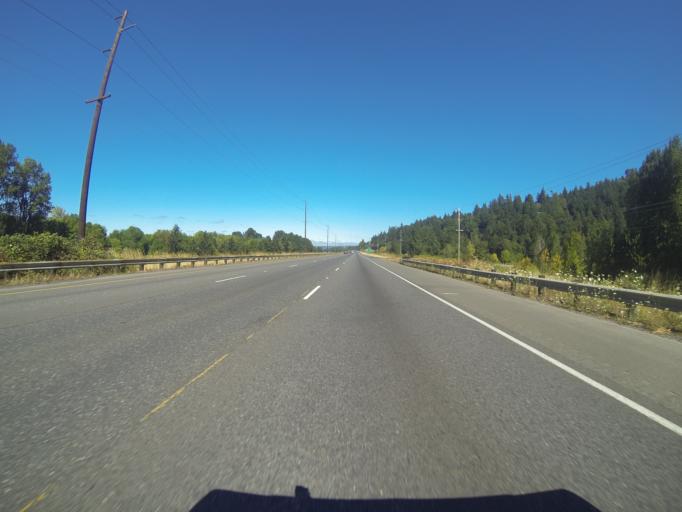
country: US
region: Washington
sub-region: Cowlitz County
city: Woodland
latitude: 45.9449
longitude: -122.7787
